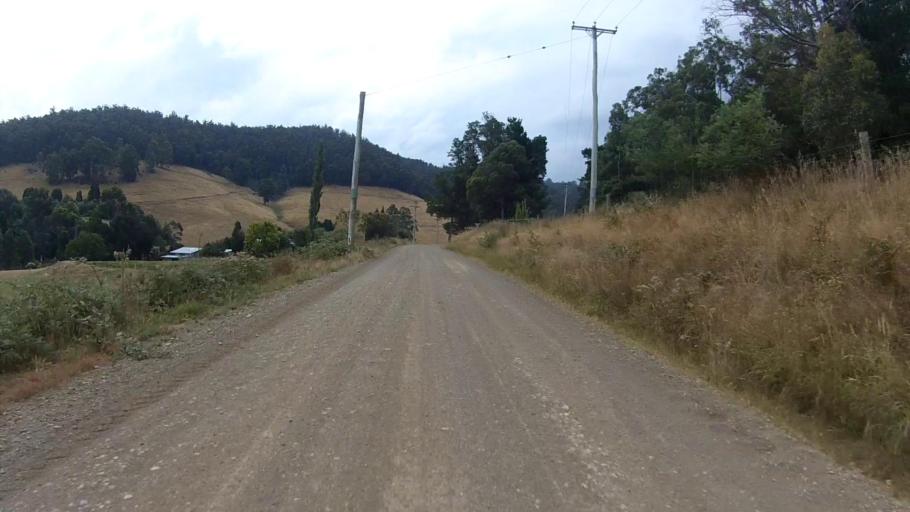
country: AU
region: Tasmania
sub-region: Huon Valley
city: Huonville
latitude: -42.9724
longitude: 147.0541
